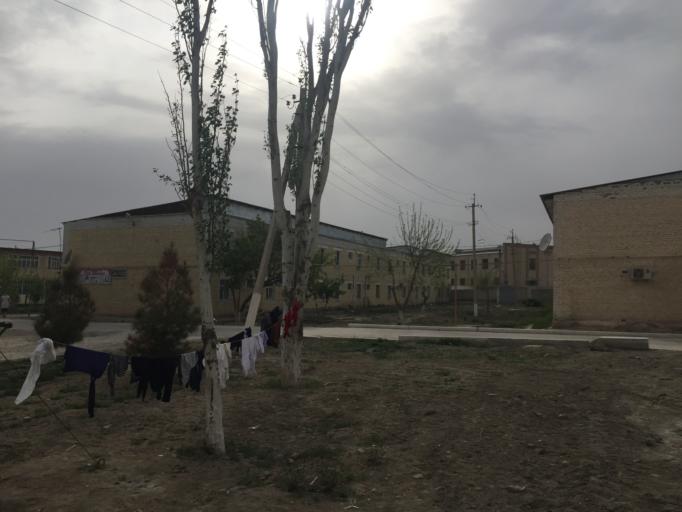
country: UZ
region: Bukhara
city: Kogon
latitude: 39.7317
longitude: 64.5296
